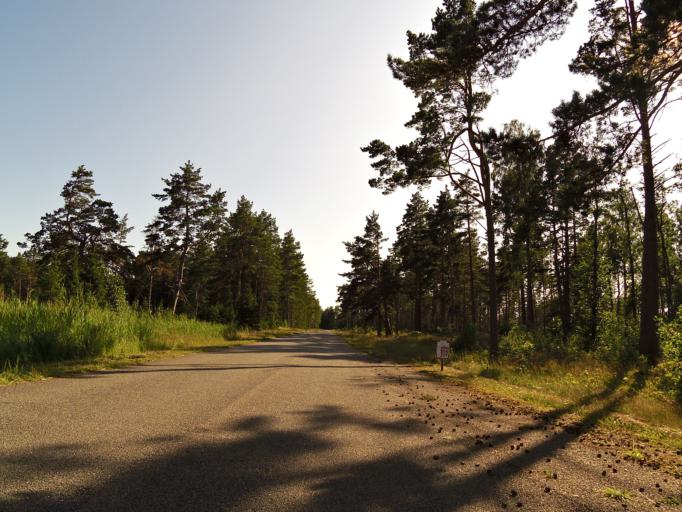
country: EE
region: Hiiumaa
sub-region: Kaerdla linn
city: Kardla
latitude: 58.8978
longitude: 22.2785
